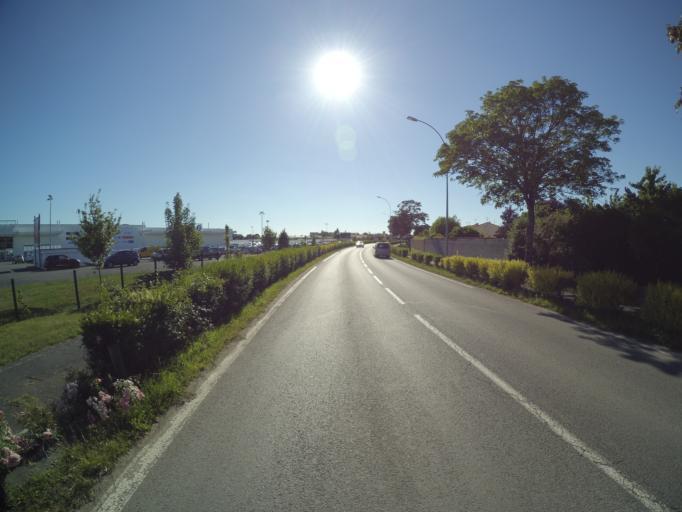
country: FR
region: Pays de la Loire
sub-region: Departement de la Vendee
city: Les Herbiers
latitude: 46.8580
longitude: -1.0119
